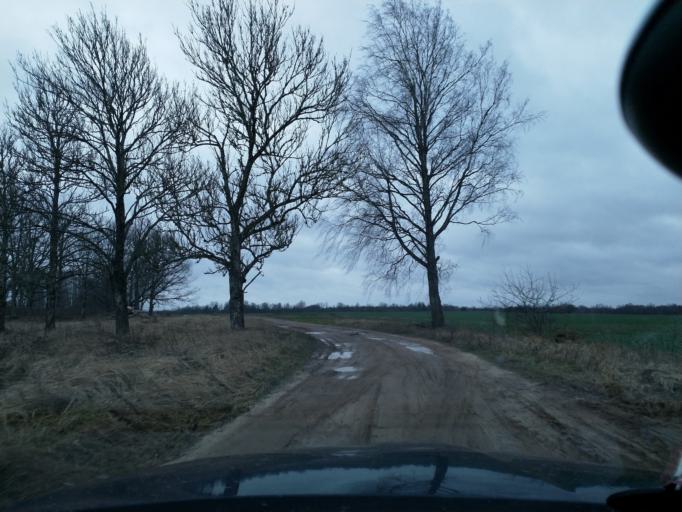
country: LV
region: Saldus Rajons
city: Saldus
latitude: 56.8944
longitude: 22.3203
